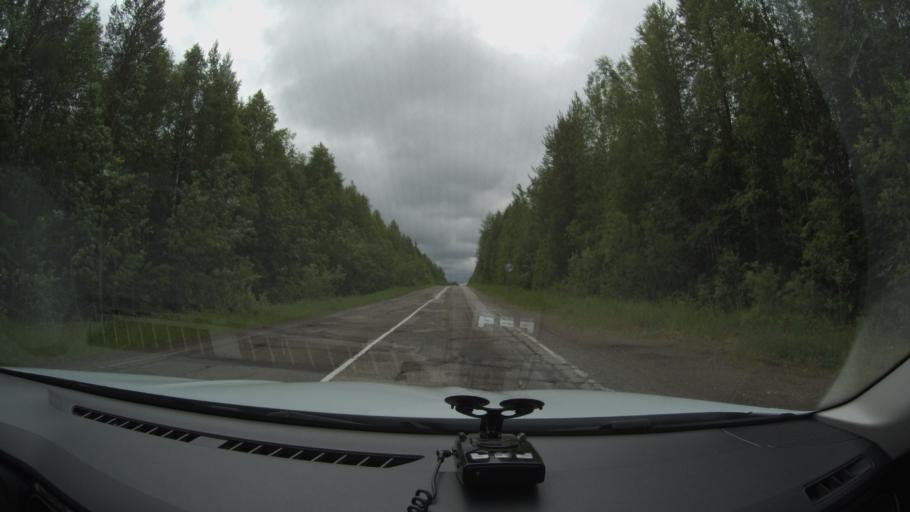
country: RU
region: Komi Republic
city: Nizhniy Odes
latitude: 63.6375
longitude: 54.6421
